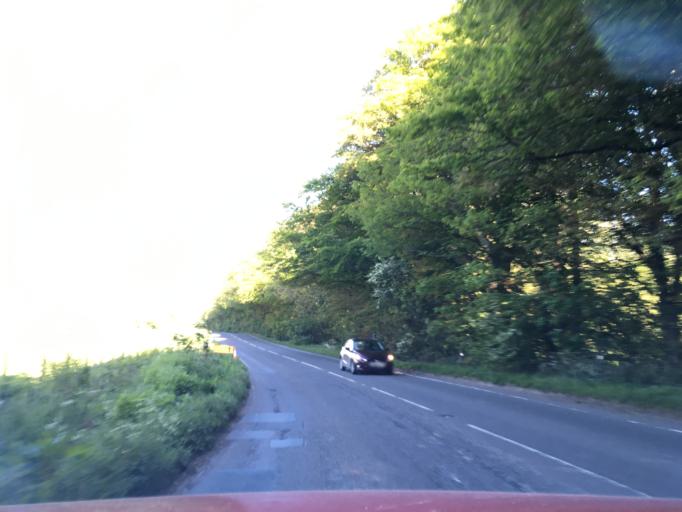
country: GB
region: England
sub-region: North Somerset
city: Easton-in-Gordano
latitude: 51.4464
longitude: -2.7080
